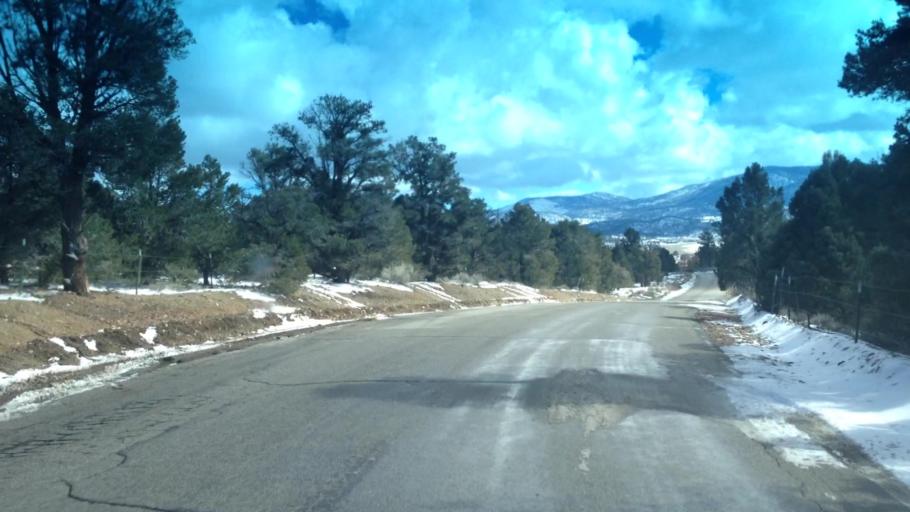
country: US
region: California
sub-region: San Bernardino County
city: Big Bear City
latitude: 34.2983
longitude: -116.8198
